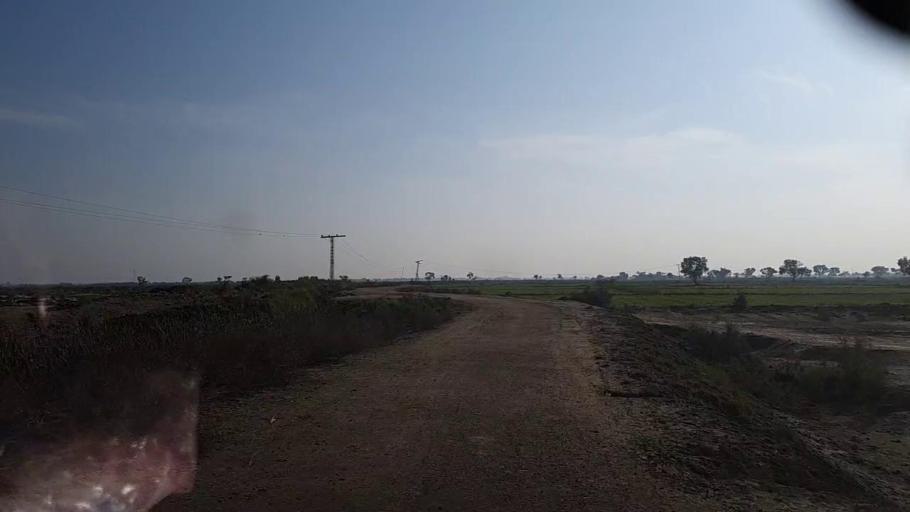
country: PK
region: Sindh
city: Jacobabad
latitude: 28.2975
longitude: 68.5578
